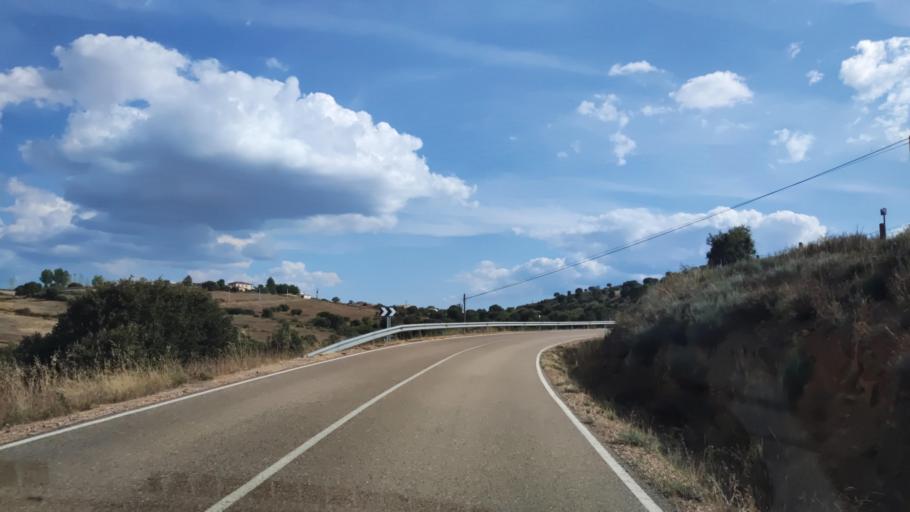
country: ES
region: Castille and Leon
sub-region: Provincia de Salamanca
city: Pastores
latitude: 40.5198
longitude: -6.5148
